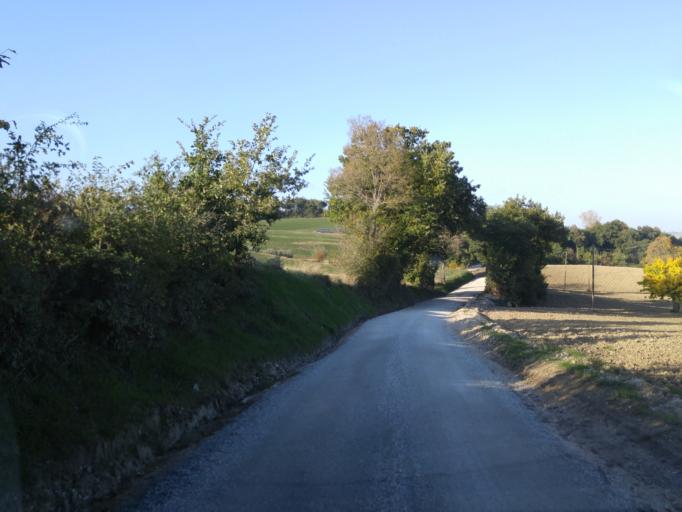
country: IT
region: The Marches
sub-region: Provincia di Pesaro e Urbino
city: Fossombrone
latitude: 43.7088
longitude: 12.8150
